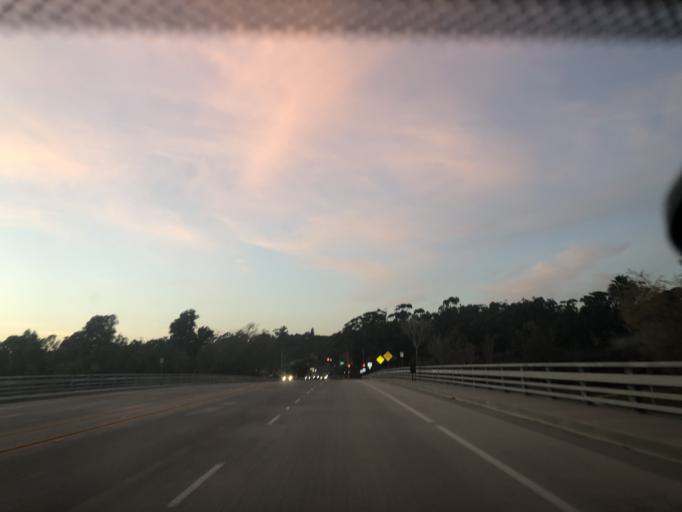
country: US
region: California
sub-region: San Diego County
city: Bonita
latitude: 32.6589
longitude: -117.0420
